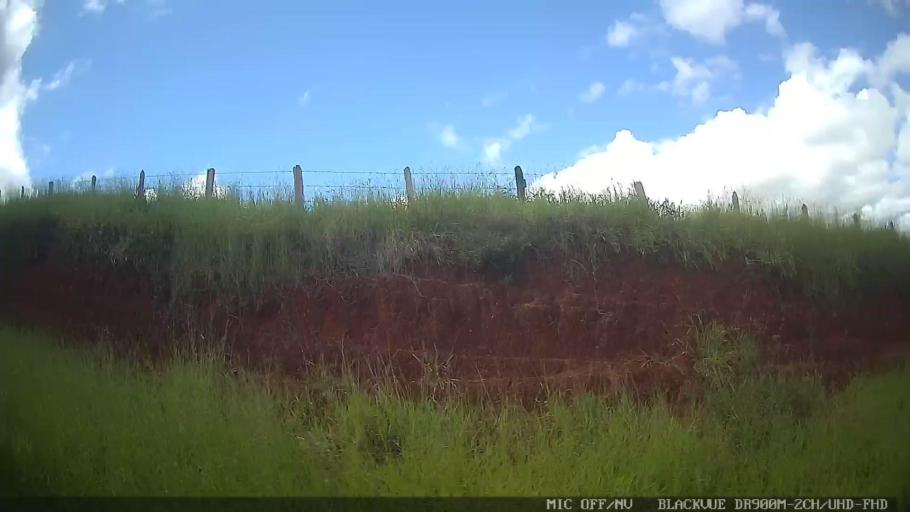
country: BR
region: Sao Paulo
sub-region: Braganca Paulista
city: Braganca Paulista
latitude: -22.8603
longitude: -46.6519
